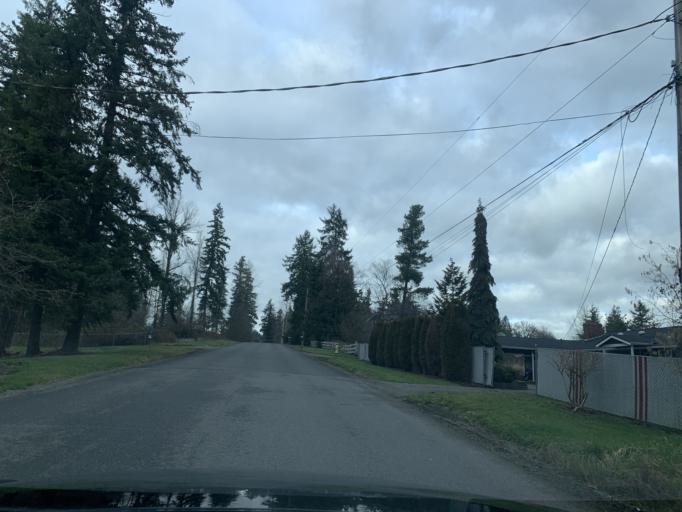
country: US
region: Washington
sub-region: Pierce County
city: Milton
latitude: 47.2397
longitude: -122.3073
